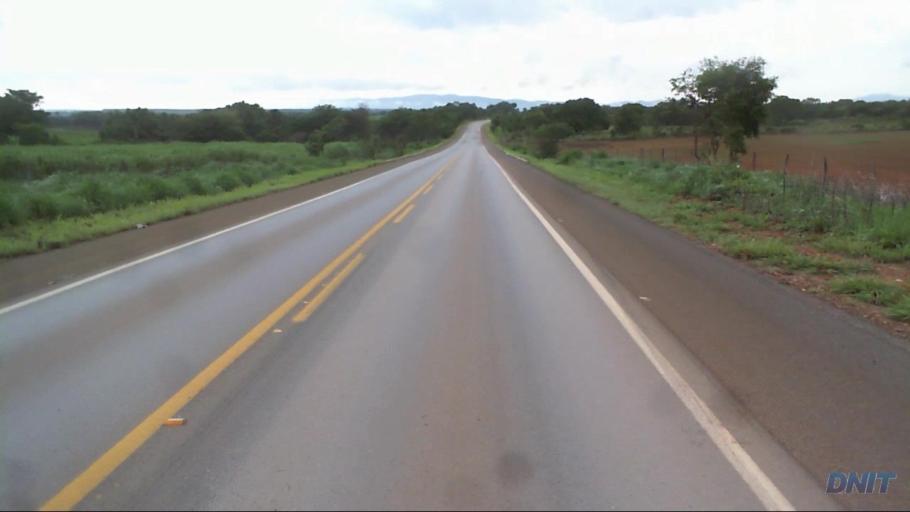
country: BR
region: Goias
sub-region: Uruacu
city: Uruacu
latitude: -14.7237
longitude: -49.0976
